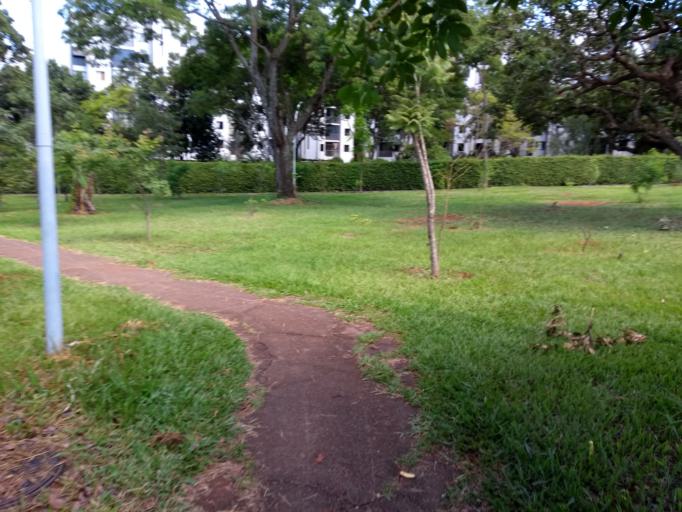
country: BR
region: Federal District
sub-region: Brasilia
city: Brasilia
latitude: -15.8035
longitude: -47.9433
